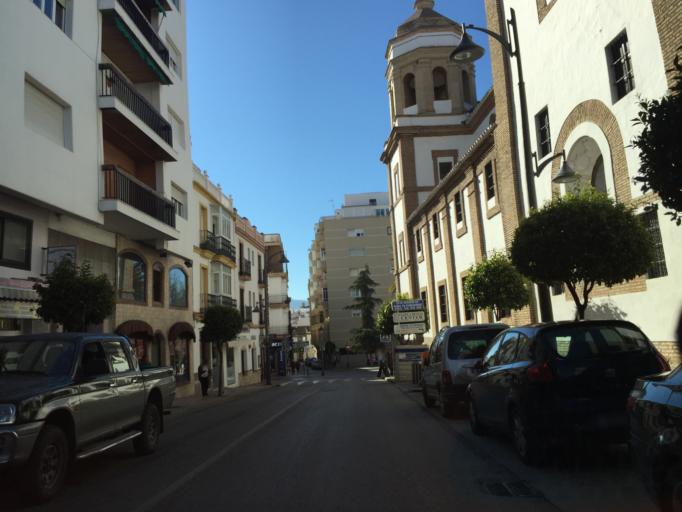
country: ES
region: Andalusia
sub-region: Provincia de Malaga
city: Ronda
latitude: 36.7448
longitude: -5.1675
